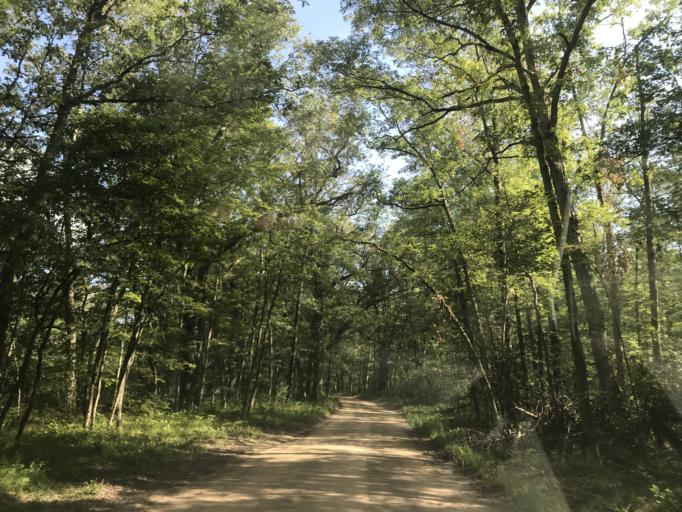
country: US
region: Michigan
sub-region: Newaygo County
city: Newaygo
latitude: 43.4648
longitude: -85.7647
